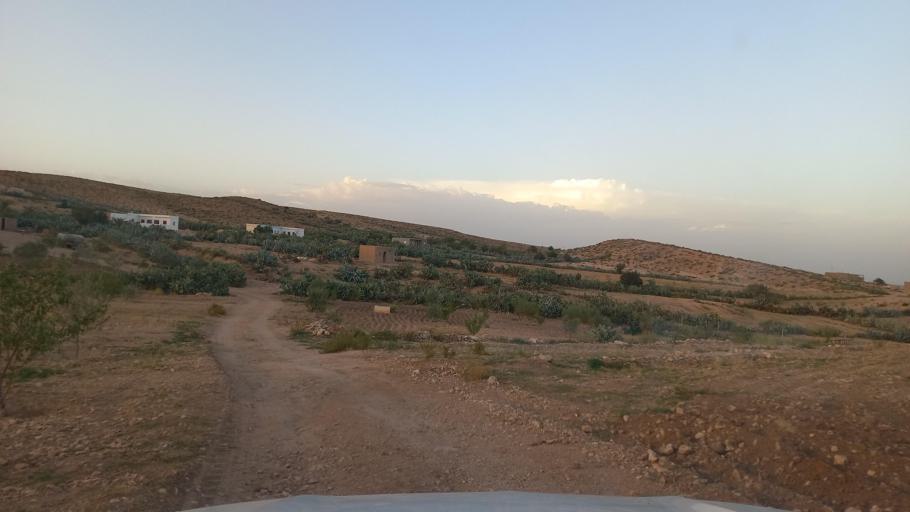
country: TN
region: Al Qasrayn
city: Sbiba
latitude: 35.3767
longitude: 9.0091
